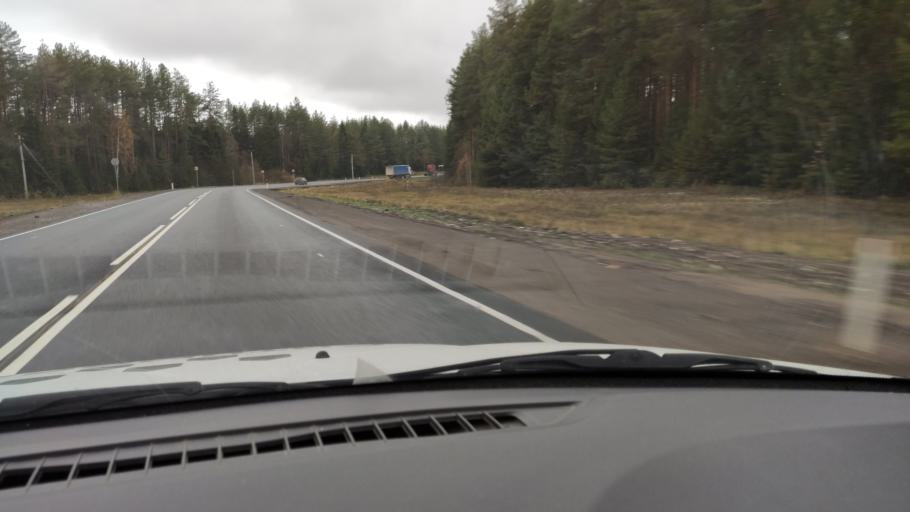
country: RU
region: Kirov
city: Belaya Kholunitsa
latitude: 58.8405
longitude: 50.7798
